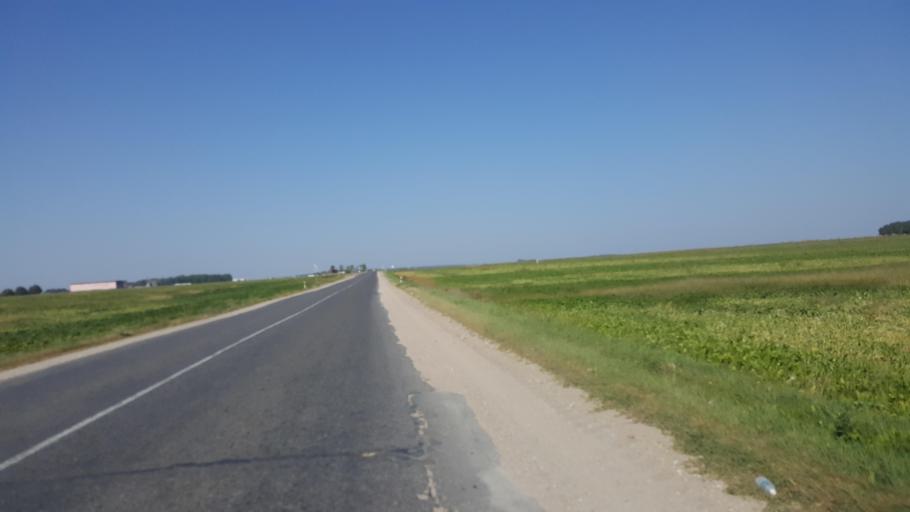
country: BY
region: Brest
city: Kamyanyets
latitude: 52.4140
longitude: 23.6414
